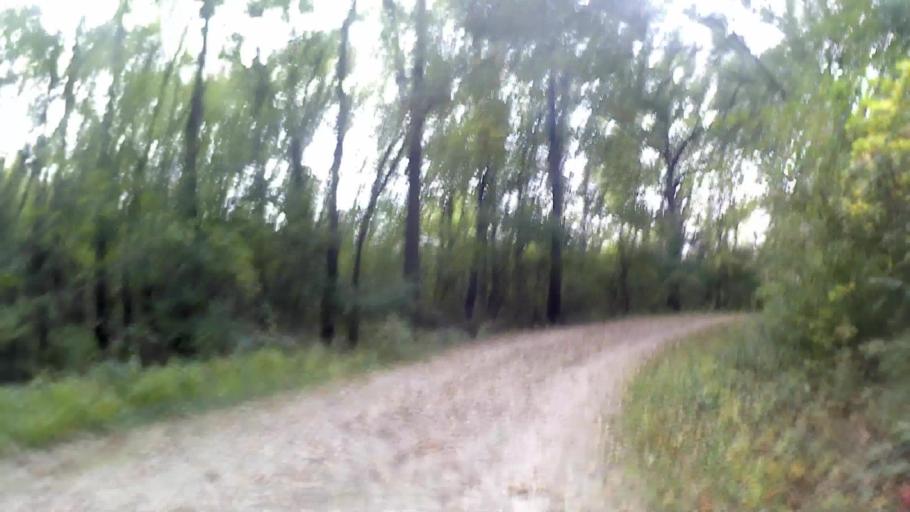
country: US
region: Illinois
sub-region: DuPage County
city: Warrenville
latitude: 41.8248
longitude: -88.1722
